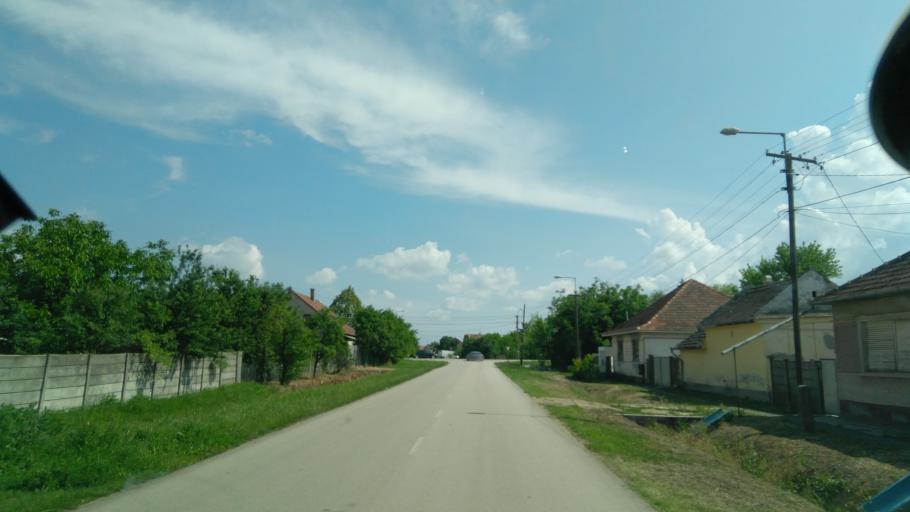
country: HU
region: Bekes
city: Doboz
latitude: 46.7342
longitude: 21.2380
